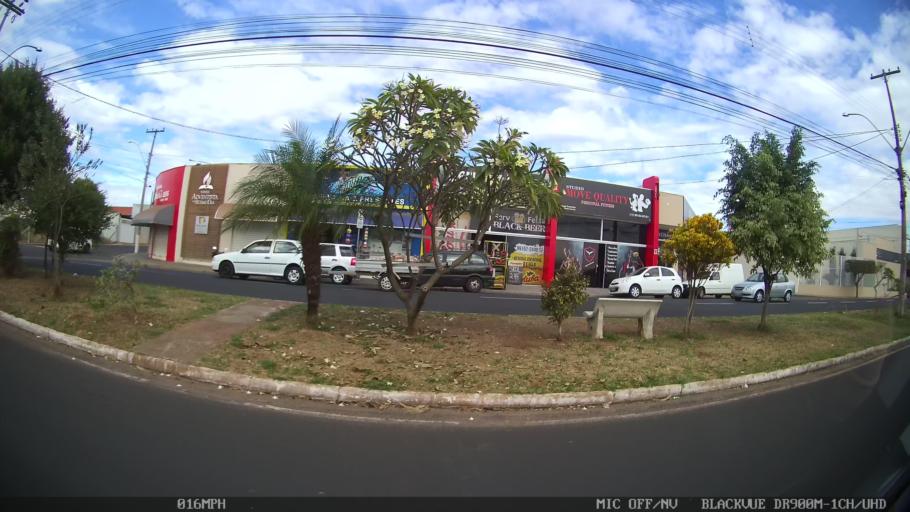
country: BR
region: Sao Paulo
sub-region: Sao Jose Do Rio Preto
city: Sao Jose do Rio Preto
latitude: -20.8047
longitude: -49.4941
